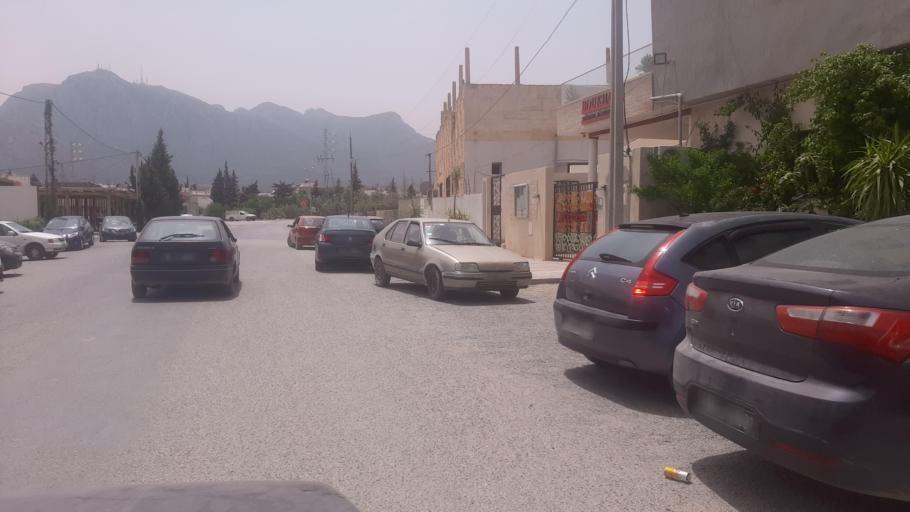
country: TN
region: Zaghwan
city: Zaghouan
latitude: 36.4141
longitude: 10.1354
